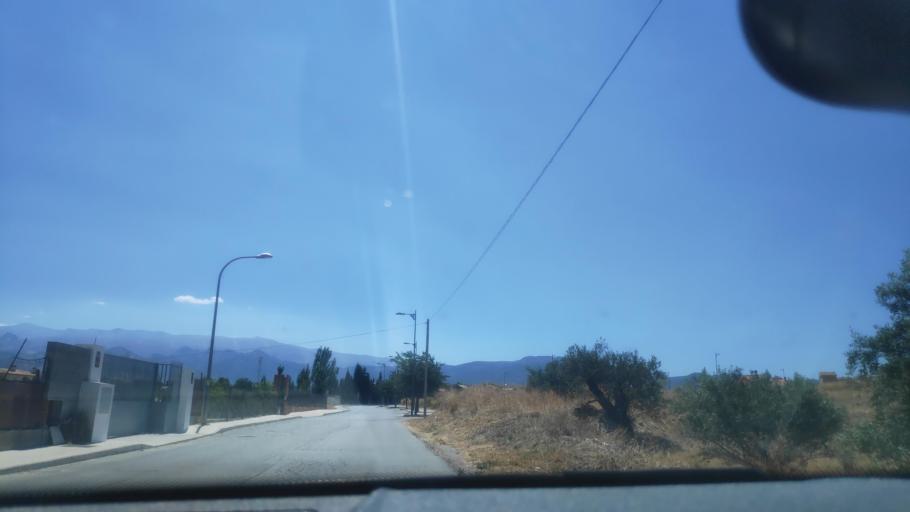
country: ES
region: Andalusia
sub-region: Provincia de Granada
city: Alhendin
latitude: 37.1036
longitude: -3.6530
